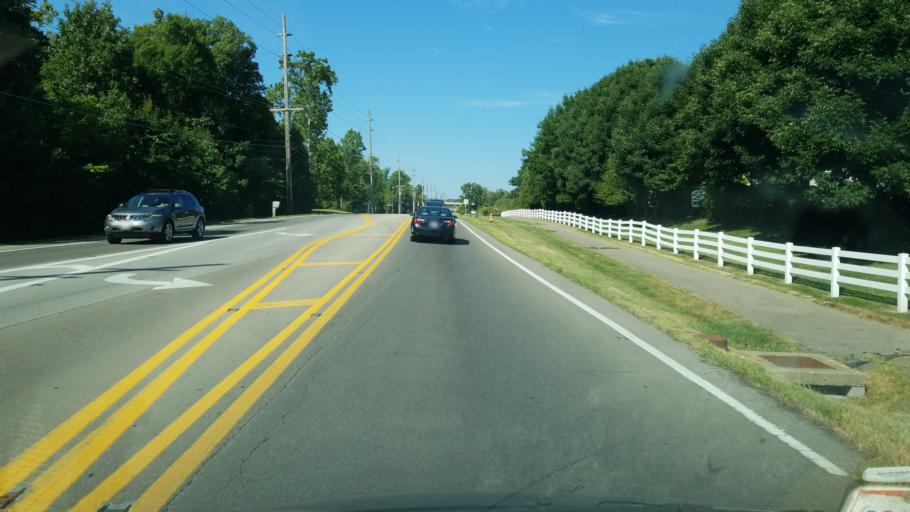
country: US
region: Ohio
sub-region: Franklin County
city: Dublin
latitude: 40.0649
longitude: -83.1255
